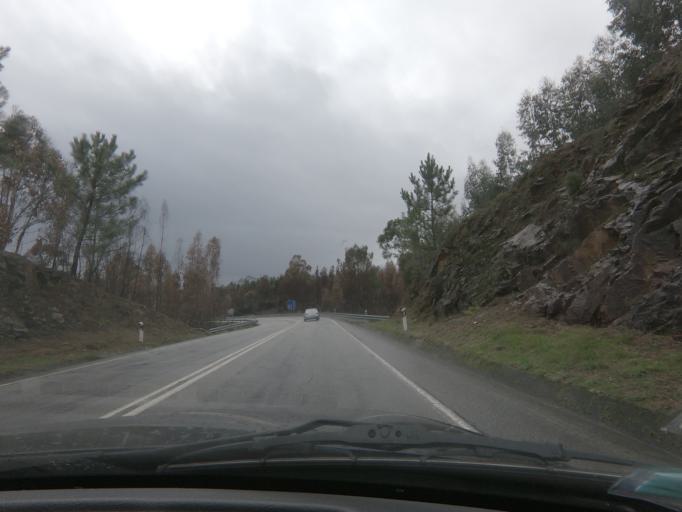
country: PT
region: Braga
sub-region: Celorico de Basto
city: Celorico de Basto
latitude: 41.3474
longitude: -8.0257
